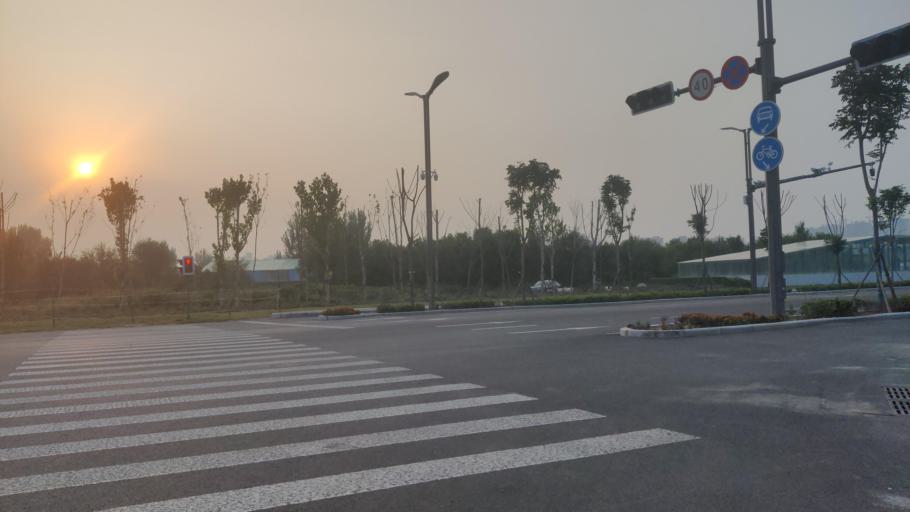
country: CN
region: Henan Sheng
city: Zhongyuanlu
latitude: 35.7628
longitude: 115.1413
